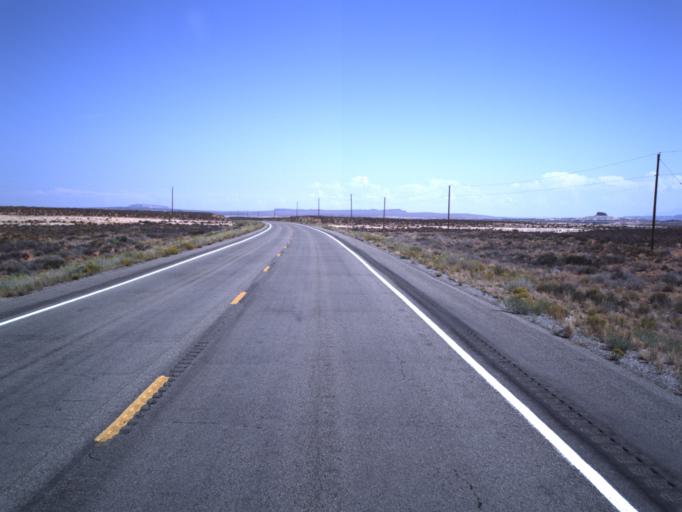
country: US
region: Utah
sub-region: San Juan County
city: Blanding
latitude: 37.0375
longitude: -109.5856
